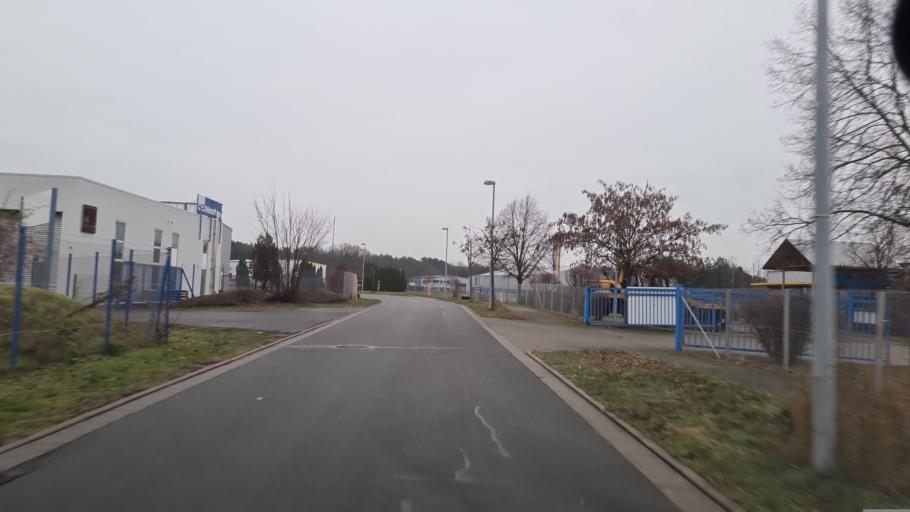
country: DE
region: Brandenburg
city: Werben
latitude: 51.7604
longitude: 14.1606
